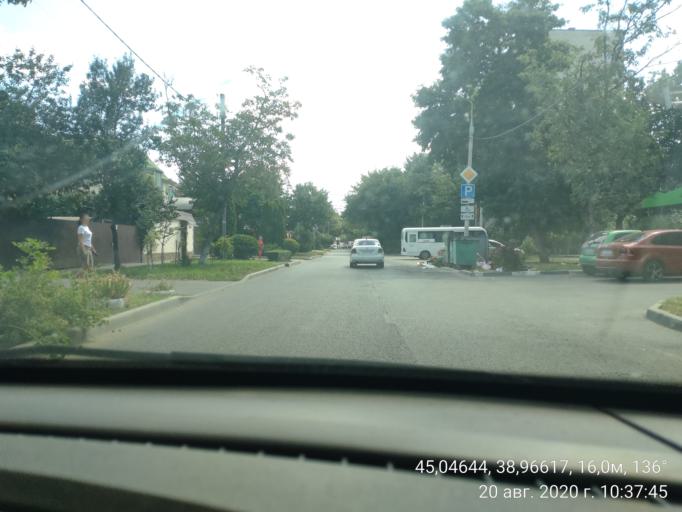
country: RU
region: Krasnodarskiy
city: Krasnodar
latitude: 45.0465
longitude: 38.9660
